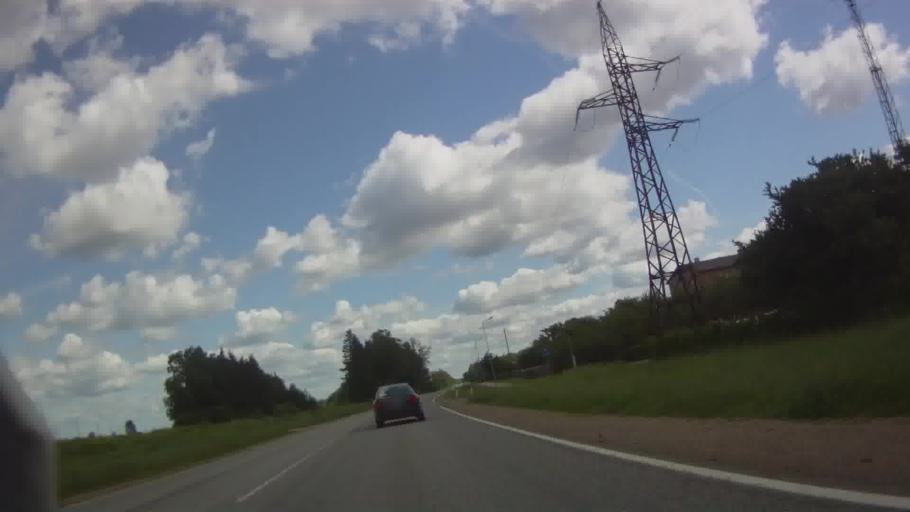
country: LV
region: Jekabpils Rajons
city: Jekabpils
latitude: 56.5237
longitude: 25.9687
